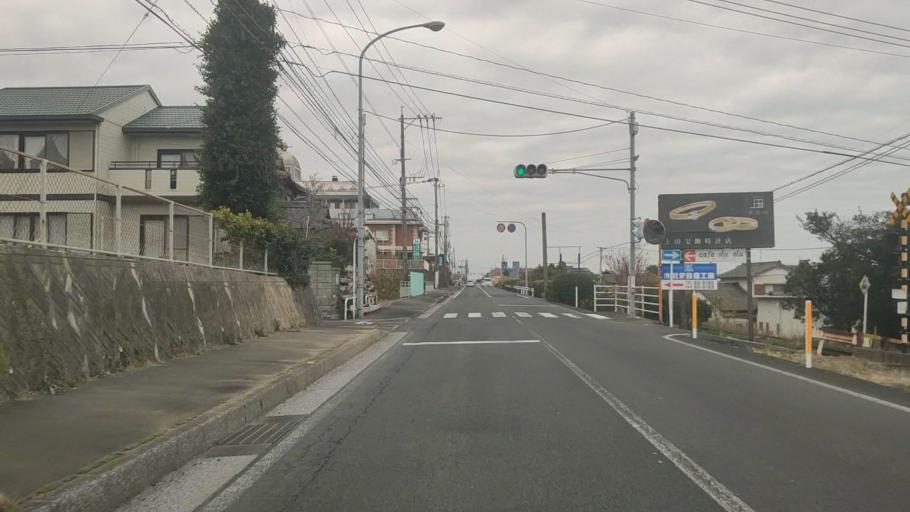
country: JP
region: Nagasaki
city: Shimabara
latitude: 32.8264
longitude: 130.3510
